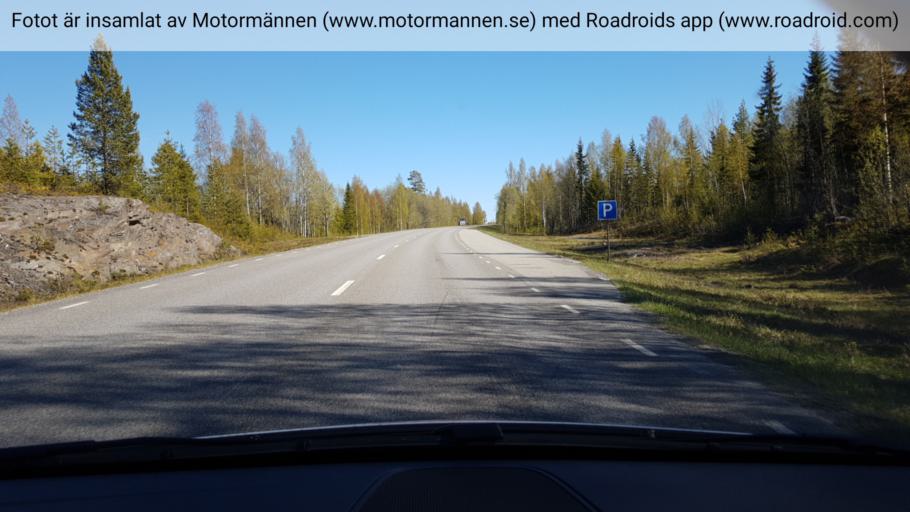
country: SE
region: Jaemtland
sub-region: Stroemsunds Kommun
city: Stroemsund
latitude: 64.3154
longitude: 15.2118
